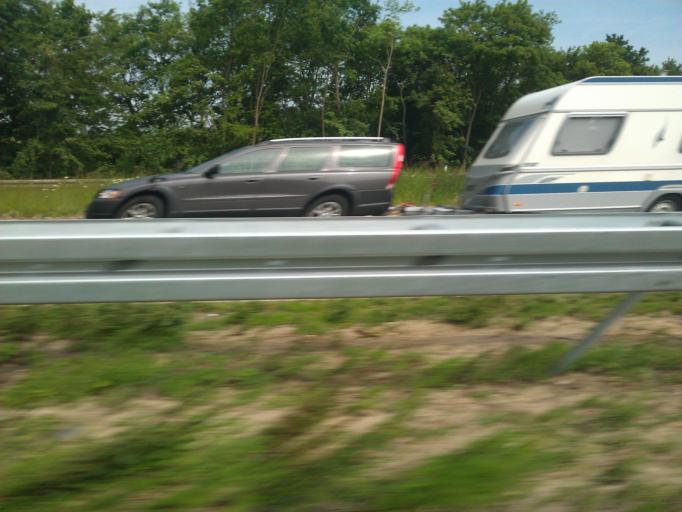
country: DE
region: North Rhine-Westphalia
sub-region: Regierungsbezirk Koln
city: Wurselen
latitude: 50.8045
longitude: 6.1070
